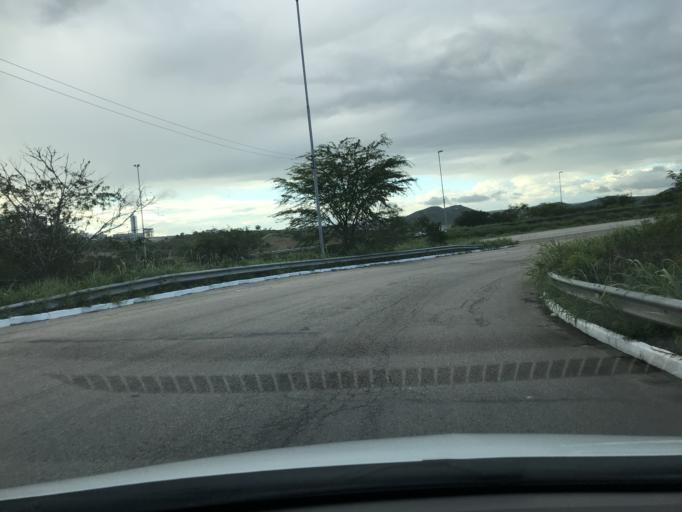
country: BR
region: Pernambuco
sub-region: Caruaru
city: Caruaru
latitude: -8.3082
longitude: -35.9434
